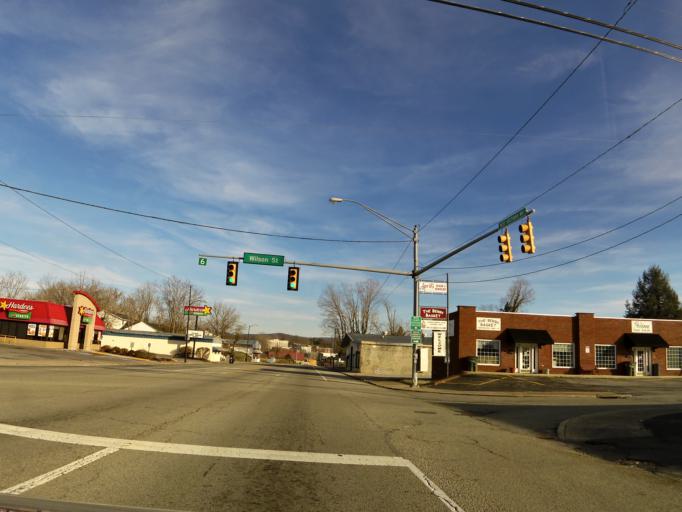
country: US
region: Tennessee
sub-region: White County
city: Sparta
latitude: 35.9288
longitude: -85.4708
